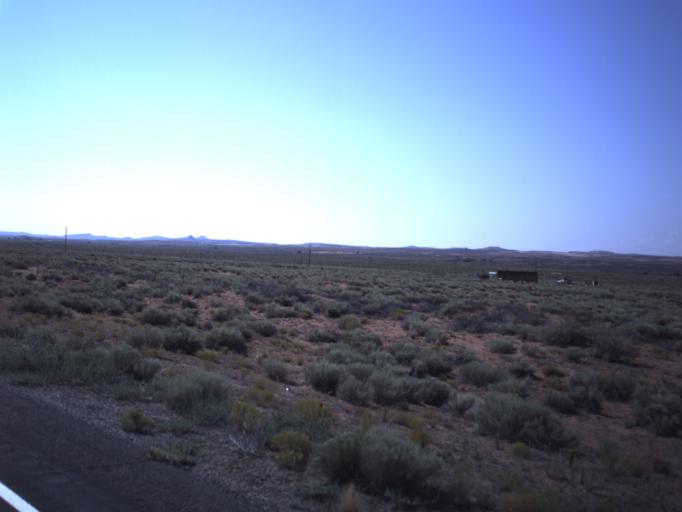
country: US
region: Utah
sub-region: San Juan County
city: Blanding
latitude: 37.1495
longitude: -109.5653
